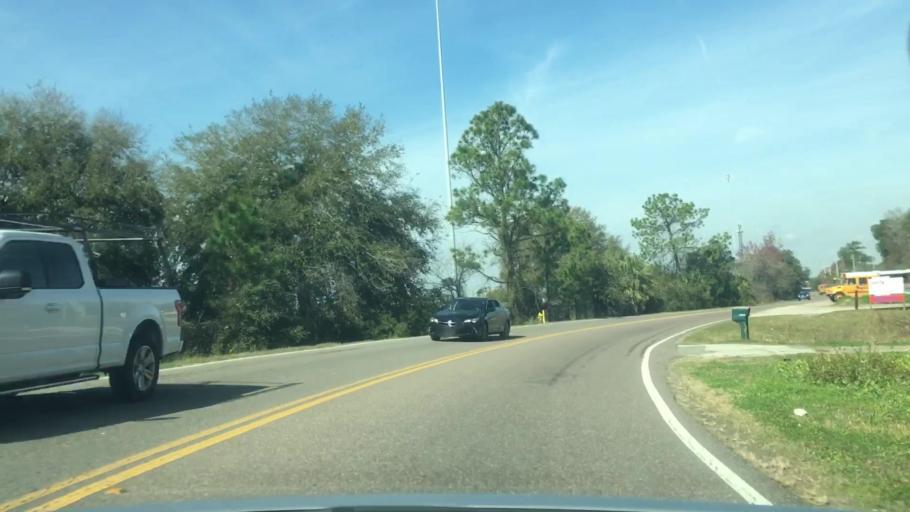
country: US
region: Florida
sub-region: Duval County
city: Jacksonville
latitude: 30.4138
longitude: -81.5636
